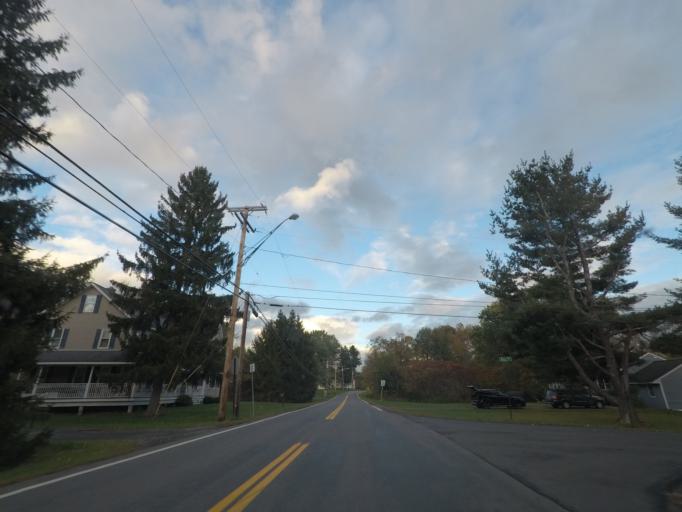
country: US
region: New York
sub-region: Rensselaer County
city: Nassau
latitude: 42.5571
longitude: -73.6255
